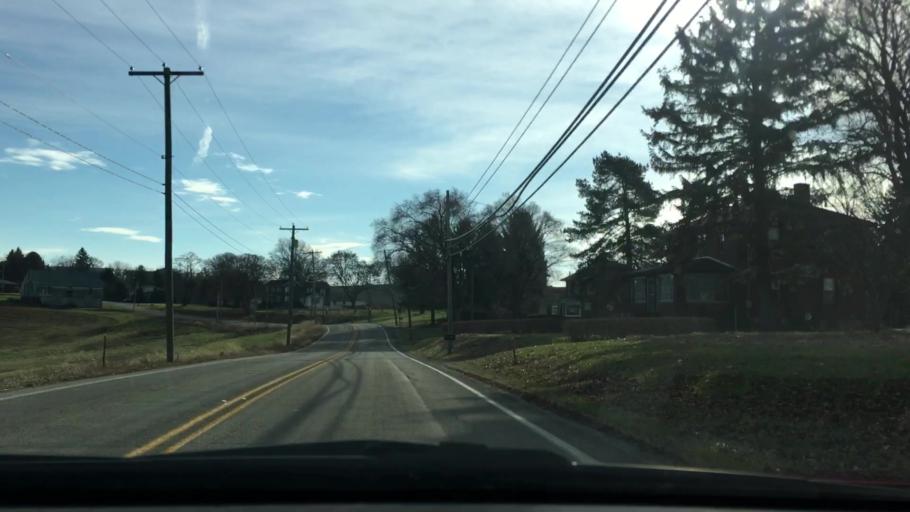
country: US
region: Pennsylvania
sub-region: Westmoreland County
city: West Newton
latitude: 40.1975
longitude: -79.7410
